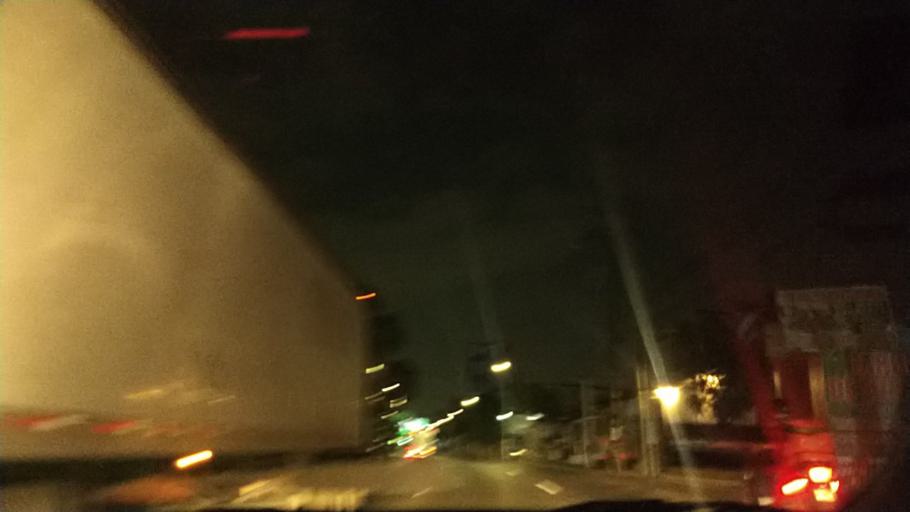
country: MX
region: Mexico
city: Ecatepec
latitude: 19.6159
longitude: -99.0627
